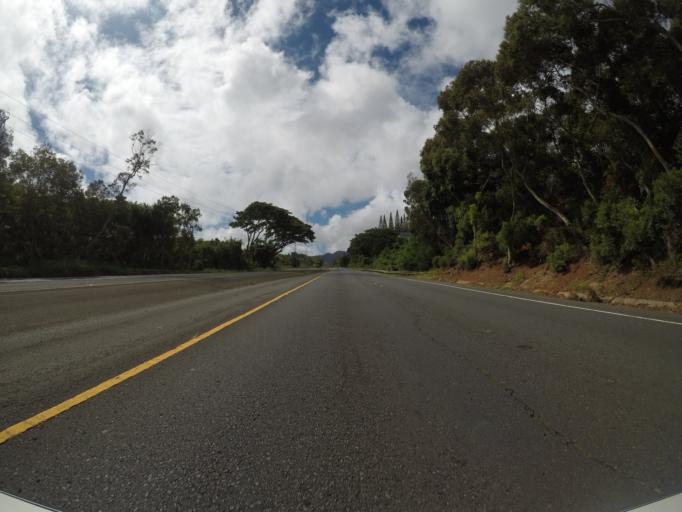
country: US
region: Hawaii
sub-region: Honolulu County
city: Waimanalo
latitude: 21.3641
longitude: -157.7377
